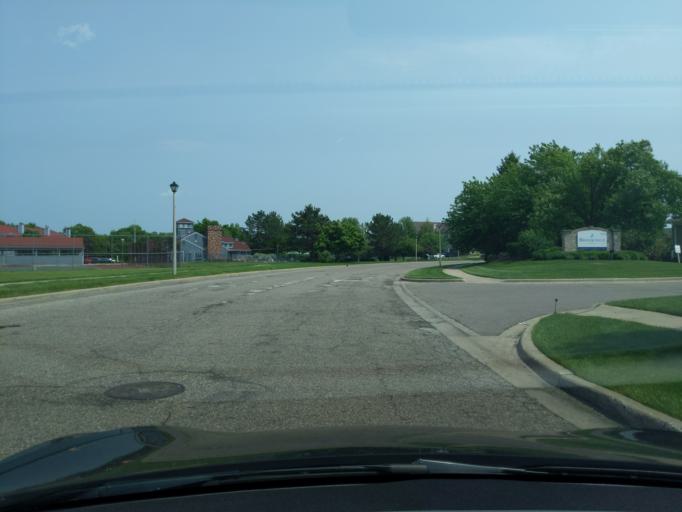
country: US
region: Michigan
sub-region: Eaton County
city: Waverly
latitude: 42.7456
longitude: -84.6572
